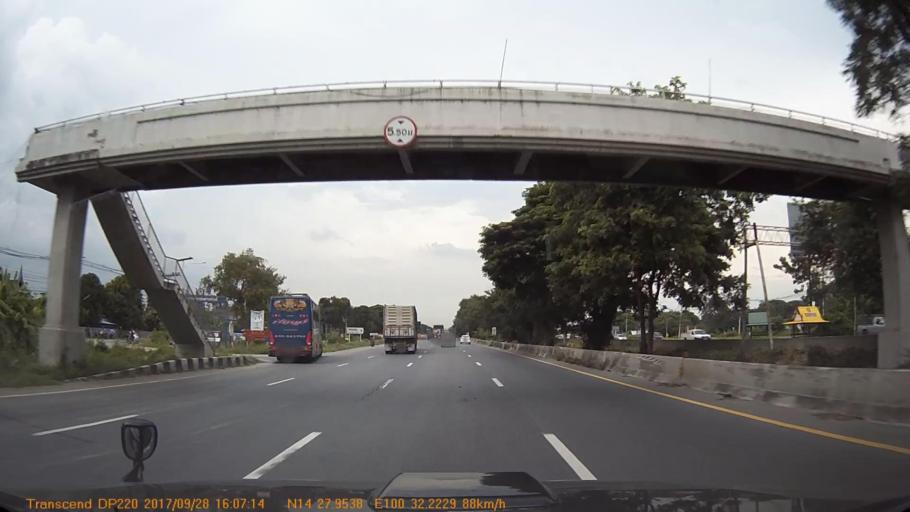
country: TH
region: Phra Nakhon Si Ayutthaya
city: Bang Pahan
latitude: 14.4659
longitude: 100.5370
